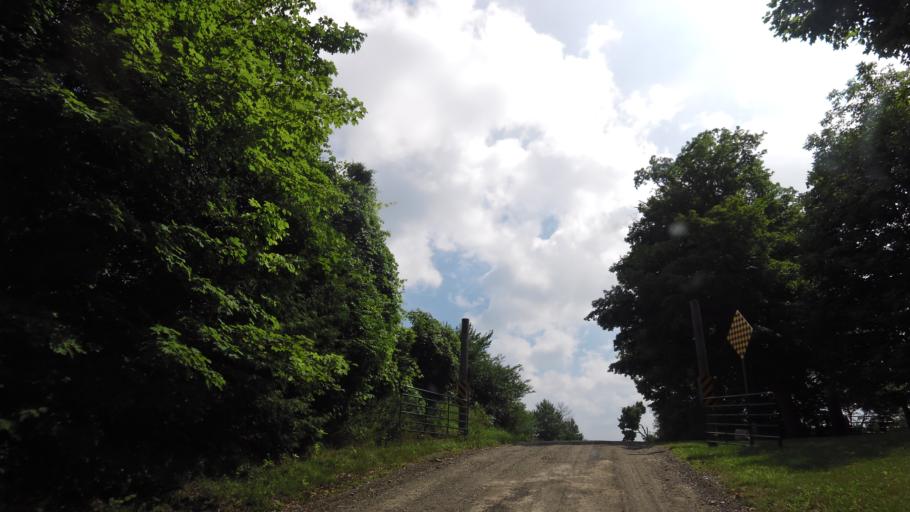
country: CA
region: Ontario
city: Oshawa
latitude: 44.0030
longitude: -78.8773
